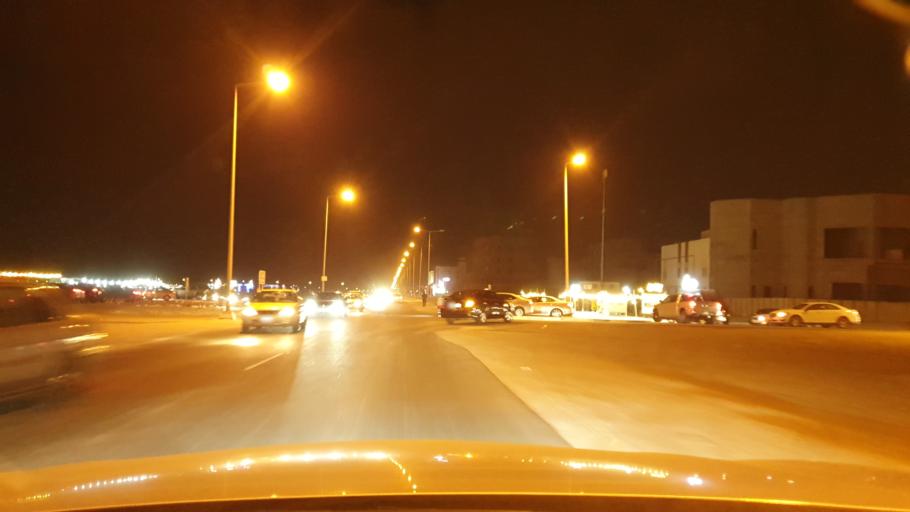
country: BH
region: Muharraq
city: Al Muharraq
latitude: 26.2663
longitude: 50.5945
